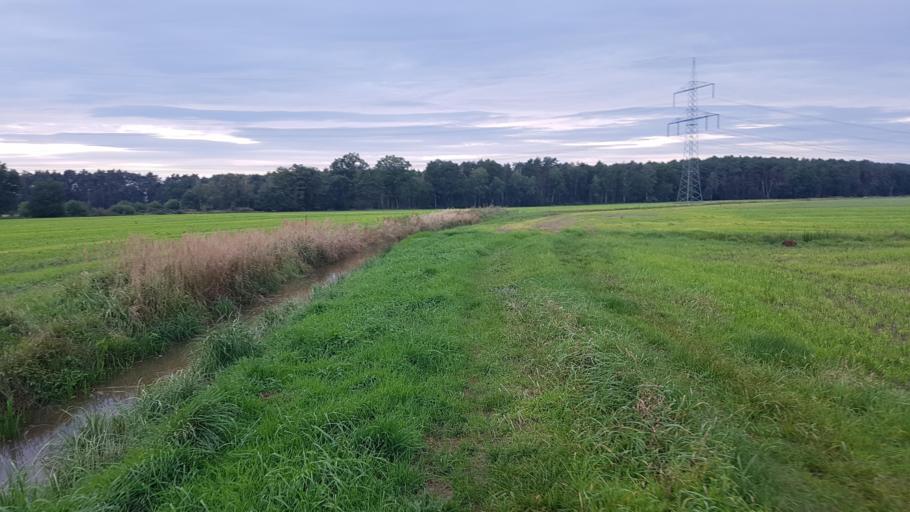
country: DE
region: Brandenburg
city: Schilda
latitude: 51.5715
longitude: 13.3904
